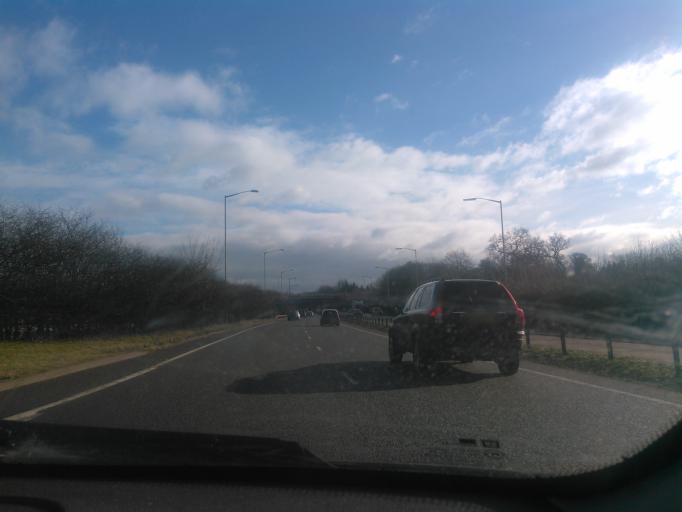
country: GB
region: England
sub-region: Staffordshire
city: Uttoxeter
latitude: 52.9122
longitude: -1.8926
